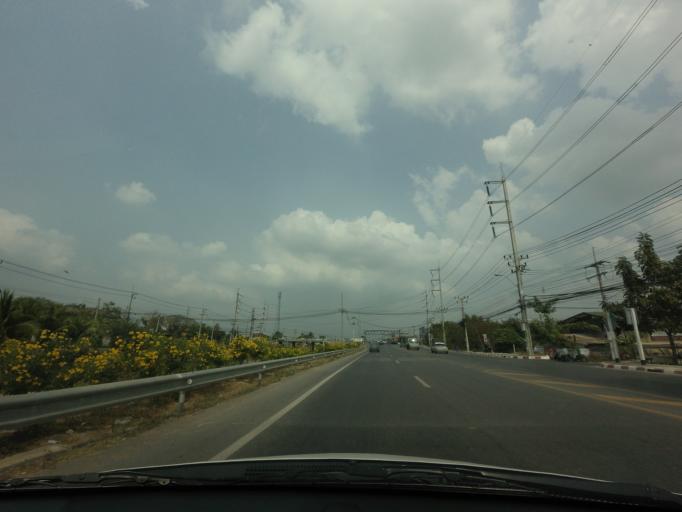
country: TH
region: Pathum Thani
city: Thanyaburi
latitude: 14.0656
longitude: 100.7102
